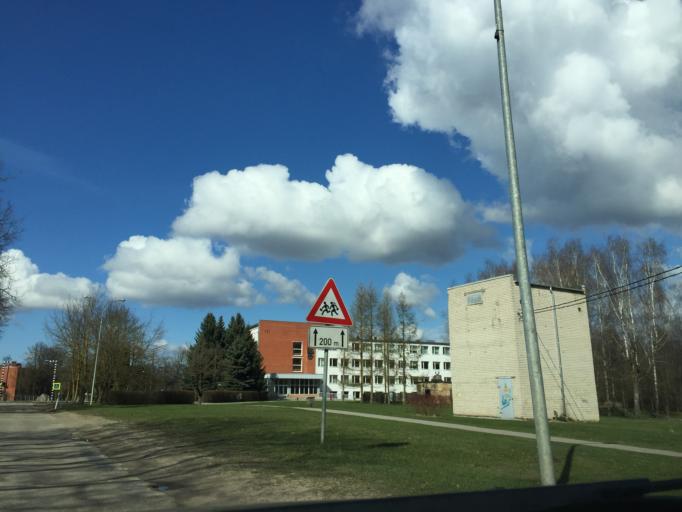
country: LV
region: Kekava
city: Kekava
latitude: 56.8256
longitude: 24.2295
